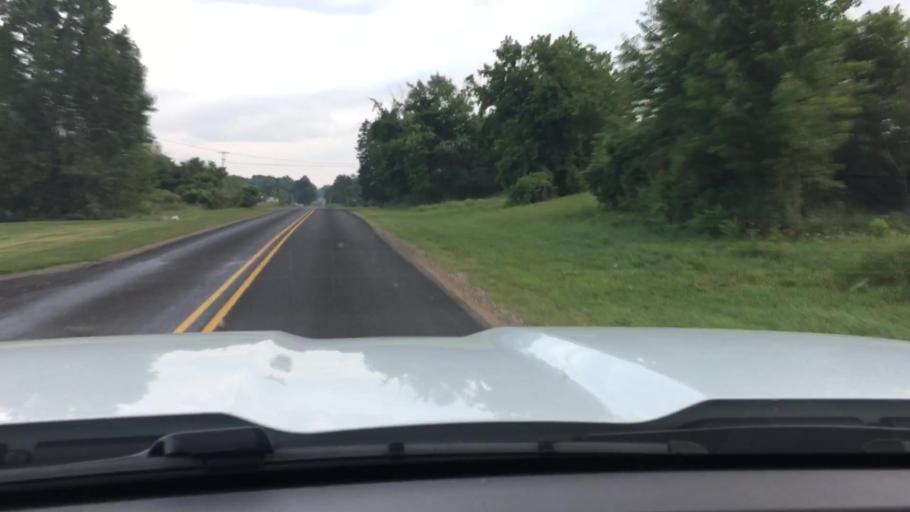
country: US
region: Michigan
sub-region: Ottawa County
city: Hudsonville
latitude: 42.8040
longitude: -85.8814
